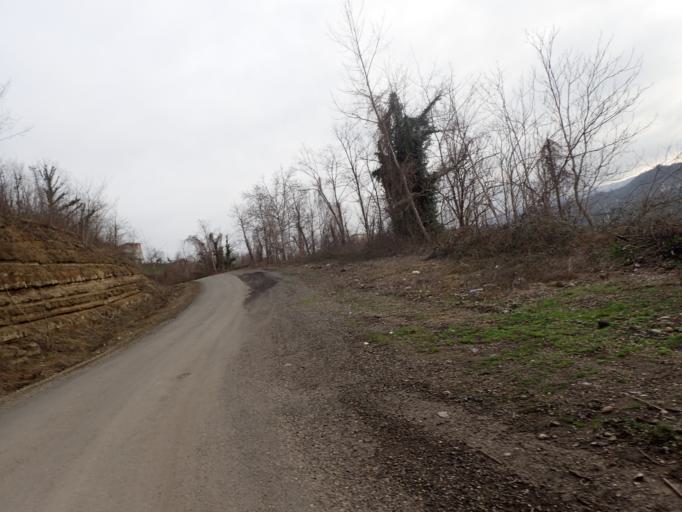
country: TR
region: Ordu
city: Camas
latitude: 40.9402
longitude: 37.5167
